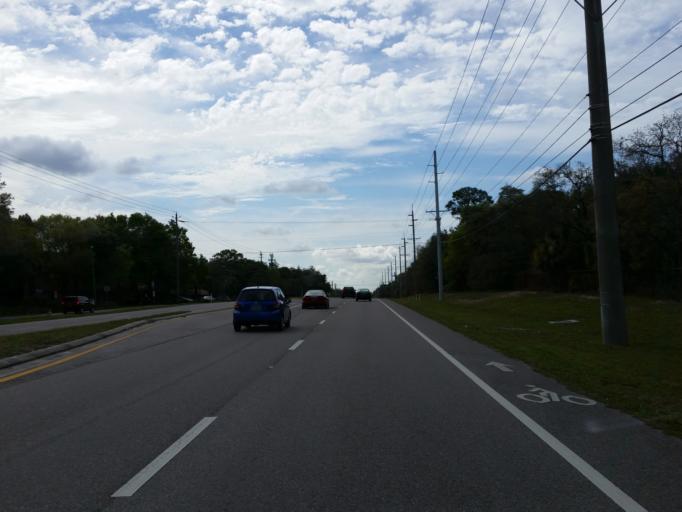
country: US
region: Florida
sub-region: Hillsborough County
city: Temple Terrace
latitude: 28.0693
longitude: -82.3877
